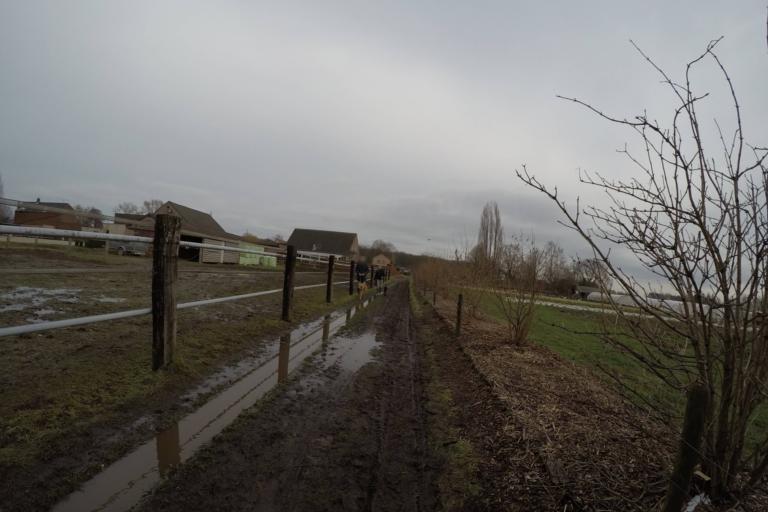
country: BE
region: Flanders
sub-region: Provincie Antwerpen
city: Wommelgem
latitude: 51.2007
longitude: 4.5449
